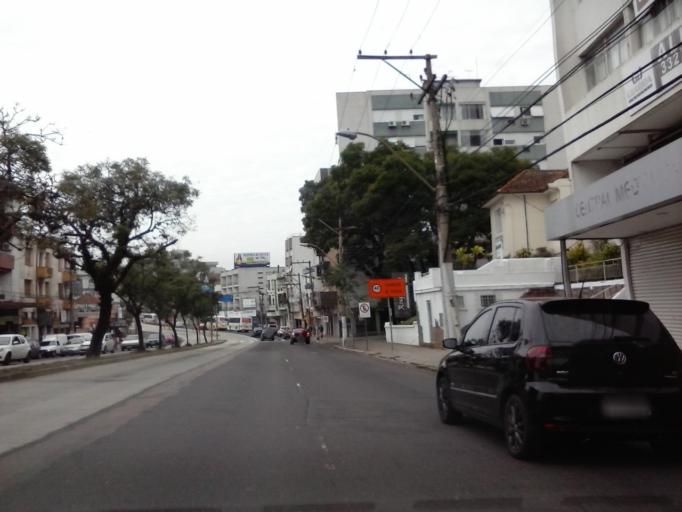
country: BR
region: Rio Grande do Sul
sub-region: Porto Alegre
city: Porto Alegre
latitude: -30.0438
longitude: -51.1863
